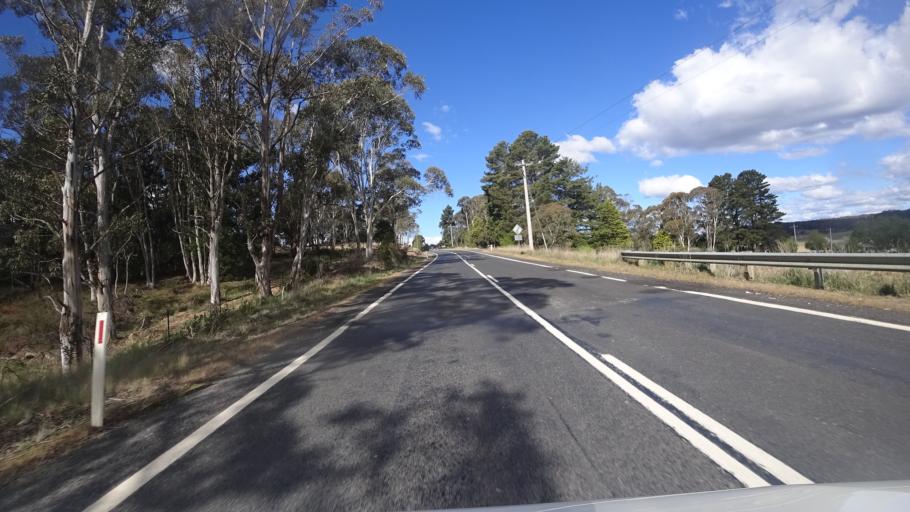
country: AU
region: New South Wales
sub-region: Oberon
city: Oberon
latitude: -33.6823
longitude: 150.0378
